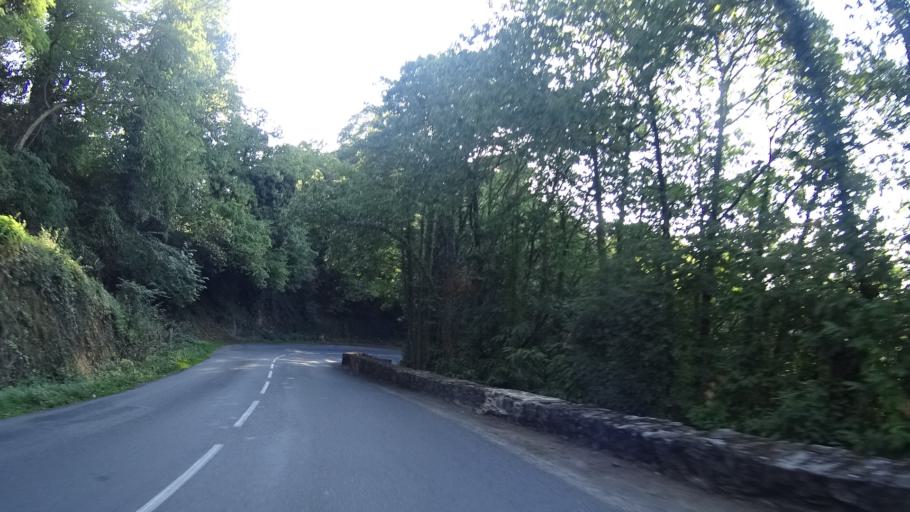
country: FR
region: Pays de la Loire
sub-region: Departement de Maine-et-Loire
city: Champtoceaux
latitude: 47.3391
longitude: -1.2684
